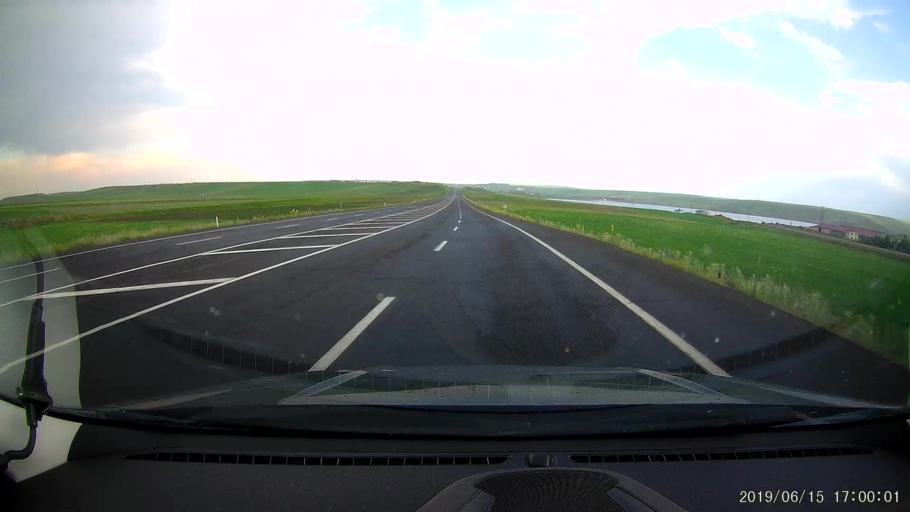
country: TR
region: Kars
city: Susuz
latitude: 40.7441
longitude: 43.1563
